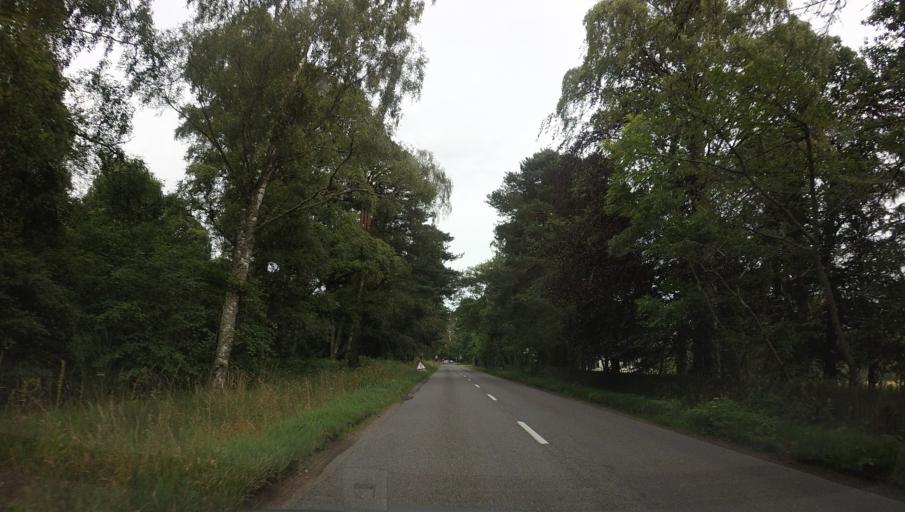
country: GB
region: Scotland
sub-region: Aberdeenshire
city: Aboyne
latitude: 57.0774
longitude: -2.8140
